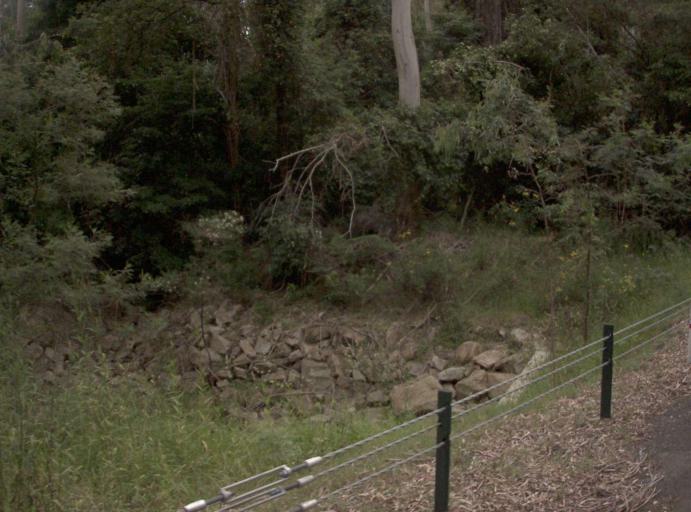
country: AU
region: New South Wales
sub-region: Bombala
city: Bombala
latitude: -37.4629
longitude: 149.1863
